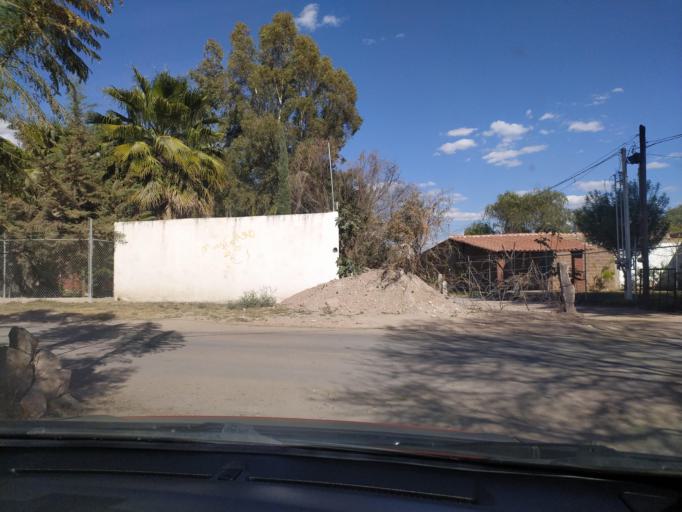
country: LA
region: Oudomxai
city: Muang La
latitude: 21.0469
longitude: 101.8357
